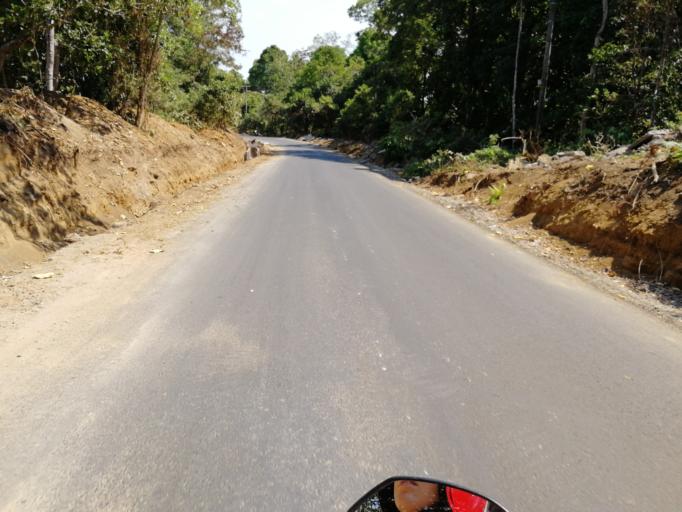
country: ID
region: West Nusa Tenggara
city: Lelongken
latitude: -8.3286
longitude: 116.4965
